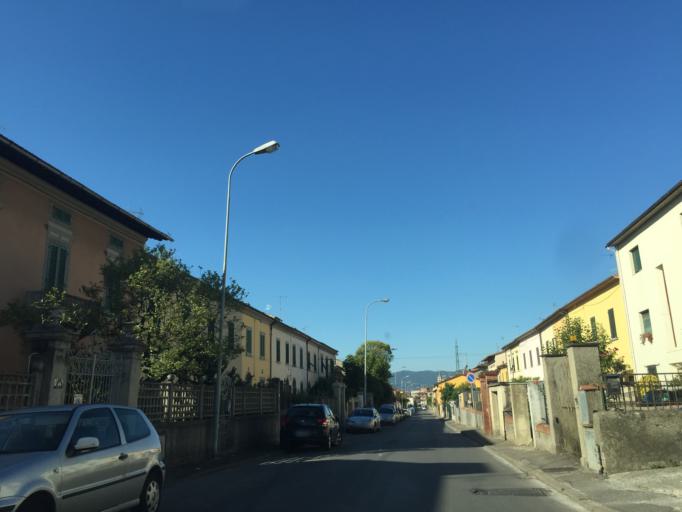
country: IT
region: Tuscany
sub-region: Provincia di Pistoia
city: Pistoia
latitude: 43.9434
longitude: 10.9299
